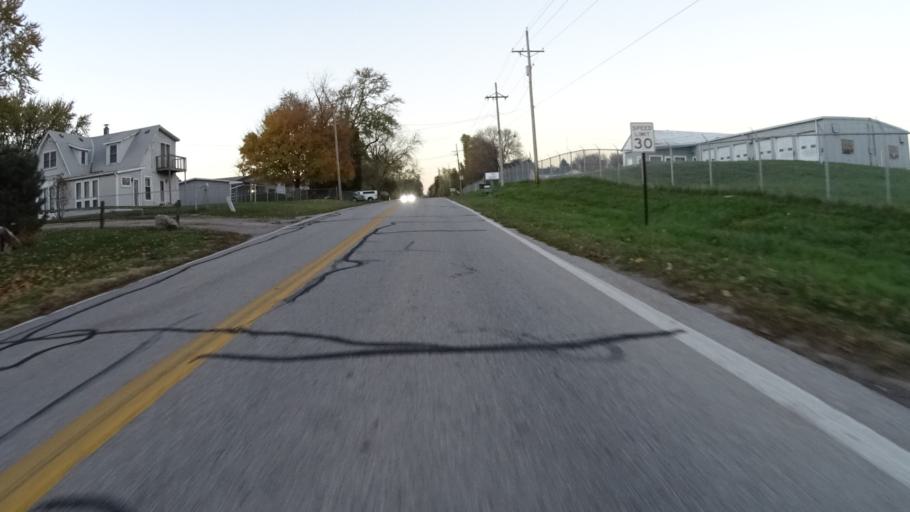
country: US
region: Nebraska
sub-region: Sarpy County
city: Offutt Air Force Base
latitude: 41.1752
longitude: -95.9527
